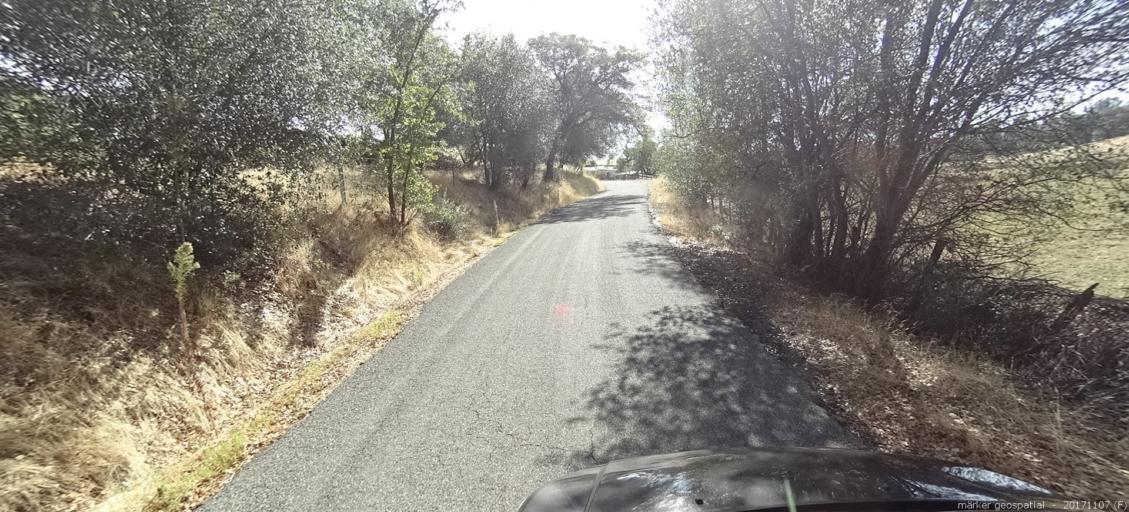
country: US
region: California
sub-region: Shasta County
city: Shasta
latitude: 40.5096
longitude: -122.5484
